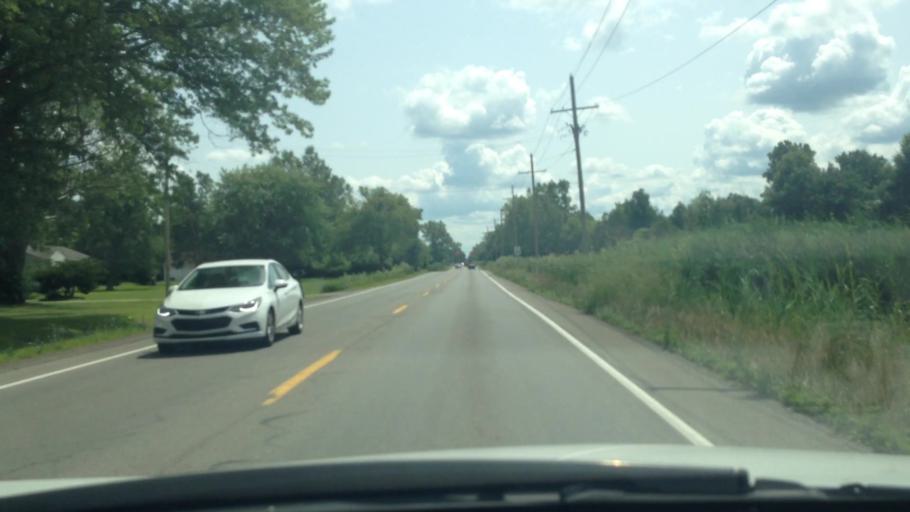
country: US
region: Michigan
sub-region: Wayne County
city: Taylor
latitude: 42.2146
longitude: -83.3072
